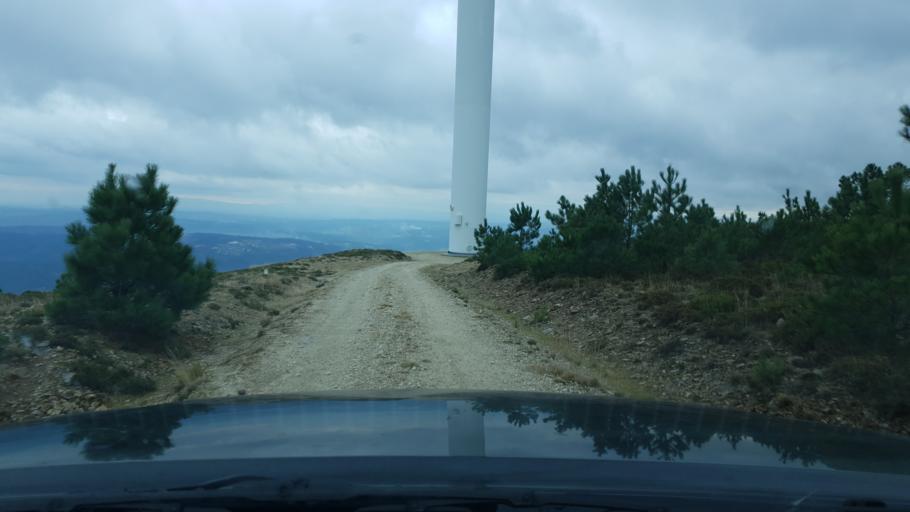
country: PT
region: Viseu
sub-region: Sao Pedro do Sul
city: Sao Pedro do Sul
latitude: 40.8653
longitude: -8.0821
